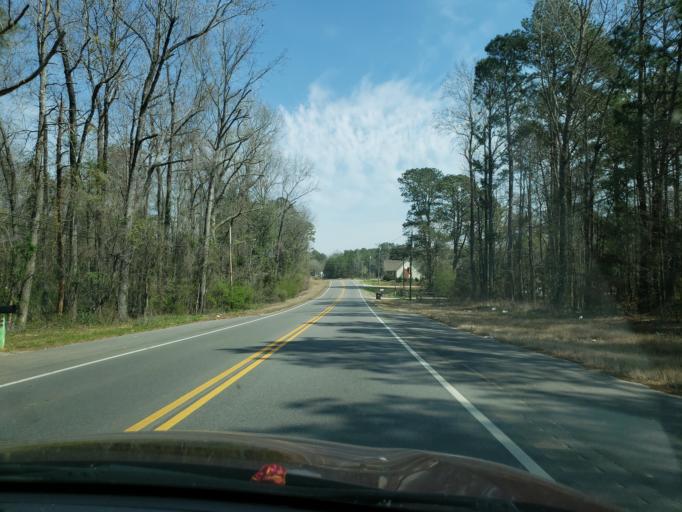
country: US
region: Alabama
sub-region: Elmore County
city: Wetumpka
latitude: 32.5570
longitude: -86.1503
